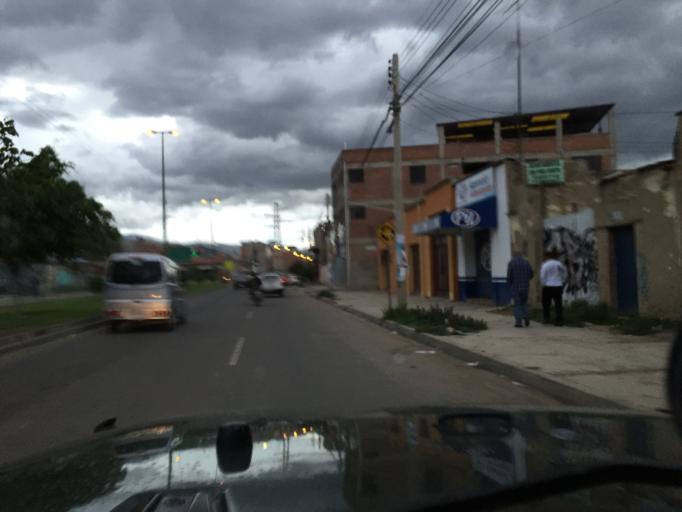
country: BO
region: Cochabamba
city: Cochabamba
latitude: -17.3964
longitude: -66.1864
